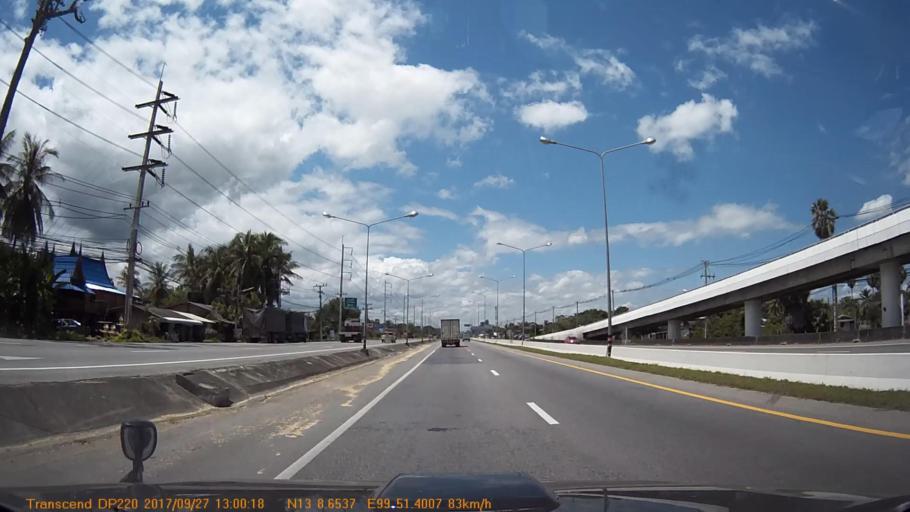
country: TH
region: Phetchaburi
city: Phetchaburi
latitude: 13.1444
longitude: 99.8565
